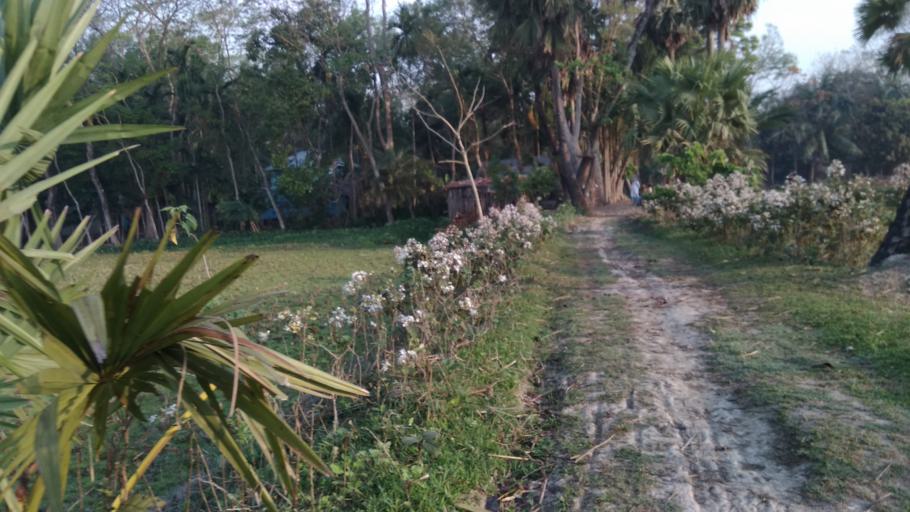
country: BD
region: Barisal
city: Mehendiganj
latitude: 22.9363
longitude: 90.4139
